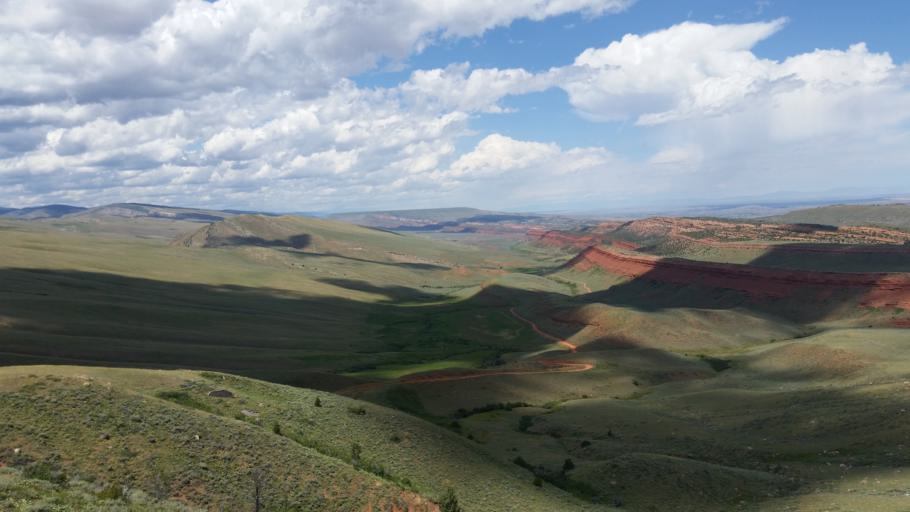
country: US
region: Wyoming
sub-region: Fremont County
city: Lander
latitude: 42.6035
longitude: -108.6136
